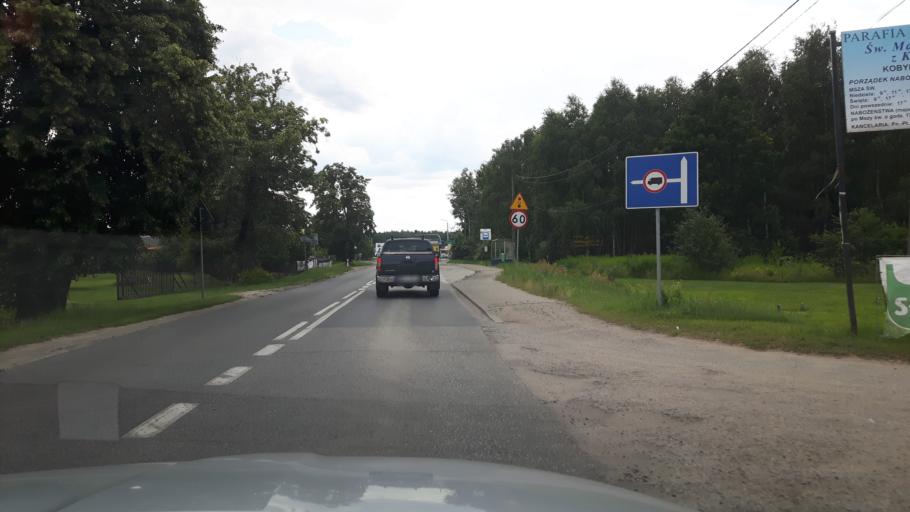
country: PL
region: Masovian Voivodeship
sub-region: Powiat wolominski
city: Kobylka
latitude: 52.3162
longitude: 21.1970
